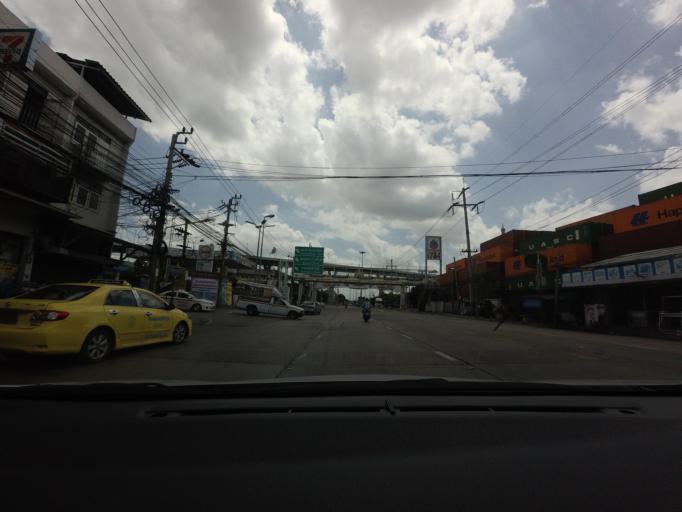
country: TH
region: Samut Prakan
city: Phra Pradaeng
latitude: 13.6543
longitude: 100.5432
